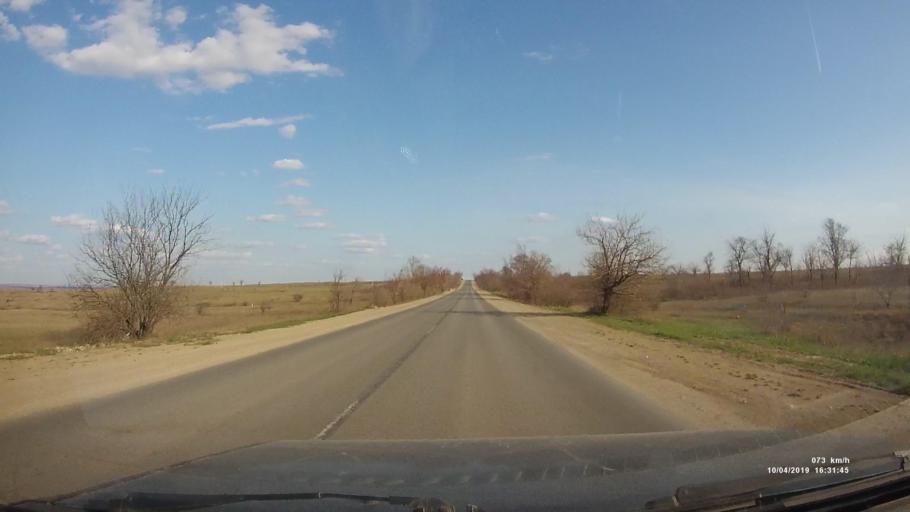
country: RU
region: Rostov
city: Staraya Stanitsa
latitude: 48.2517
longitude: 40.3795
